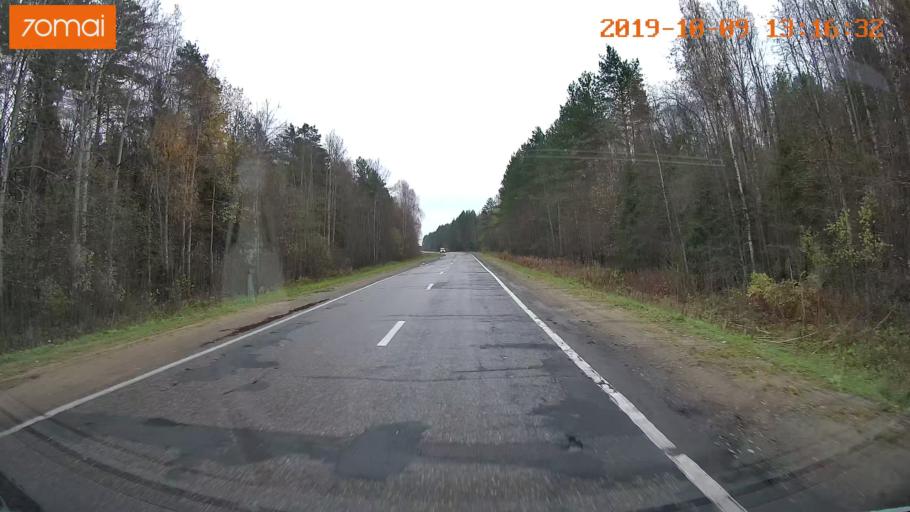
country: RU
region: Jaroslavl
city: Lyubim
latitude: 58.3606
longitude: 40.7672
